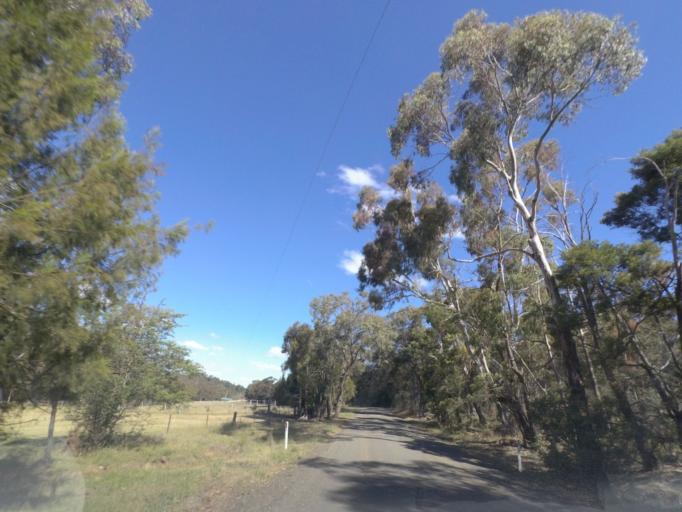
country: AU
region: Victoria
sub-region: Hume
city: Sunbury
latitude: -37.4326
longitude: 144.6579
